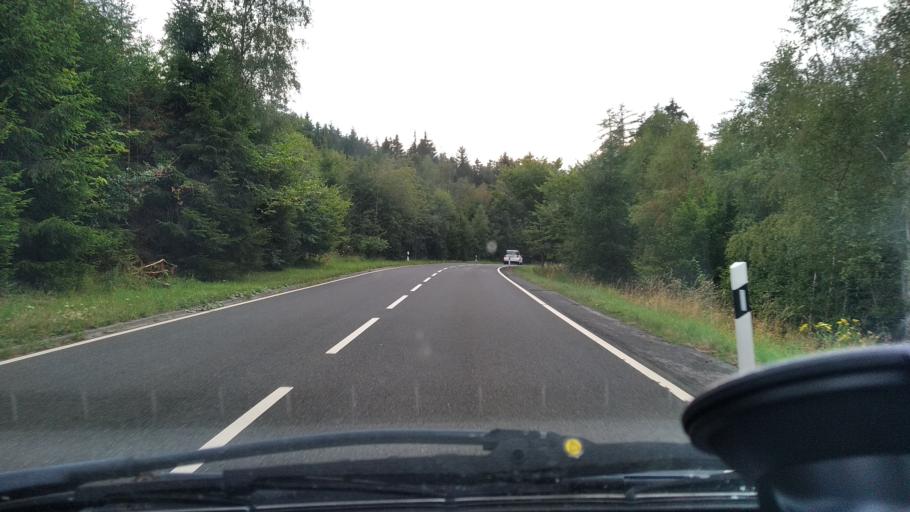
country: DE
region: Hesse
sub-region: Regierungsbezirk Giessen
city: Haiger
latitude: 50.8487
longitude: 8.2178
